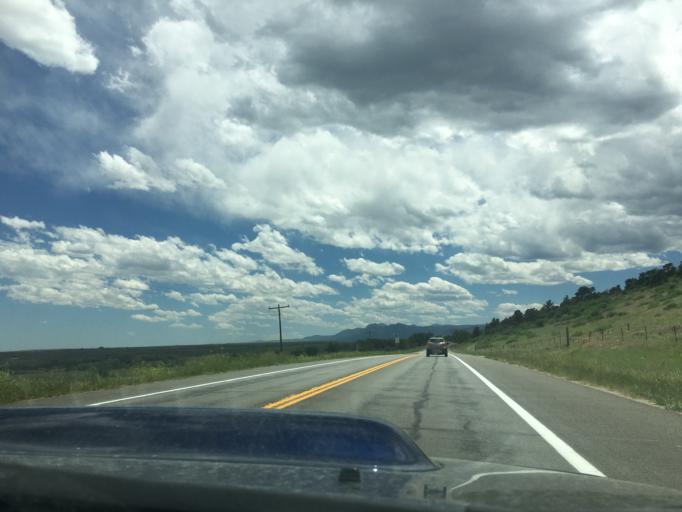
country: US
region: Colorado
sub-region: Boulder County
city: Lyons
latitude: 40.1831
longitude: -105.2530
